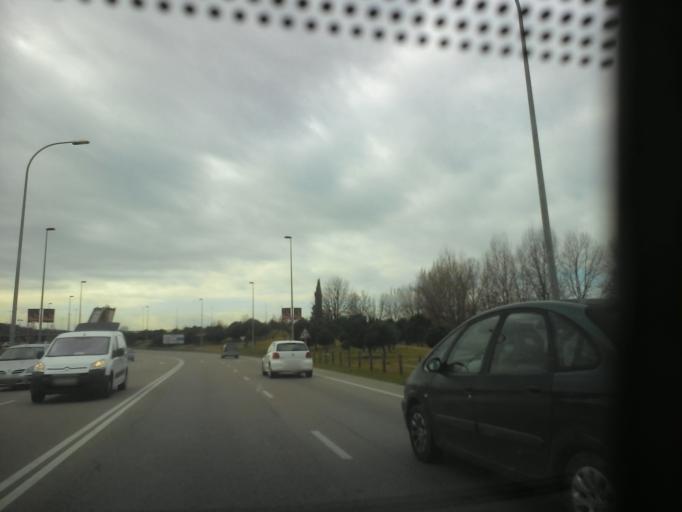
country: ES
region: Catalonia
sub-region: Provincia de Girona
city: Salt
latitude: 41.9593
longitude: 2.8101
